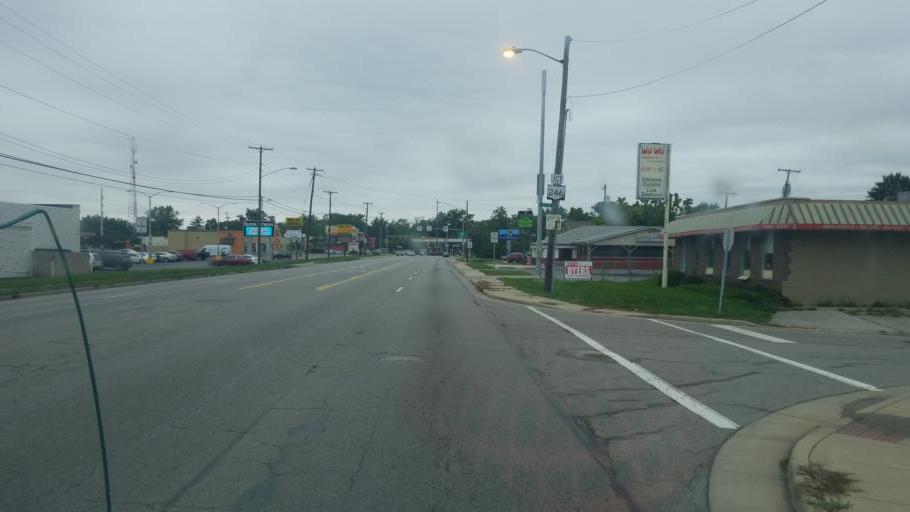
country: US
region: Ohio
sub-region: Lucas County
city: Ottawa Hills
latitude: 41.6509
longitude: -83.6646
